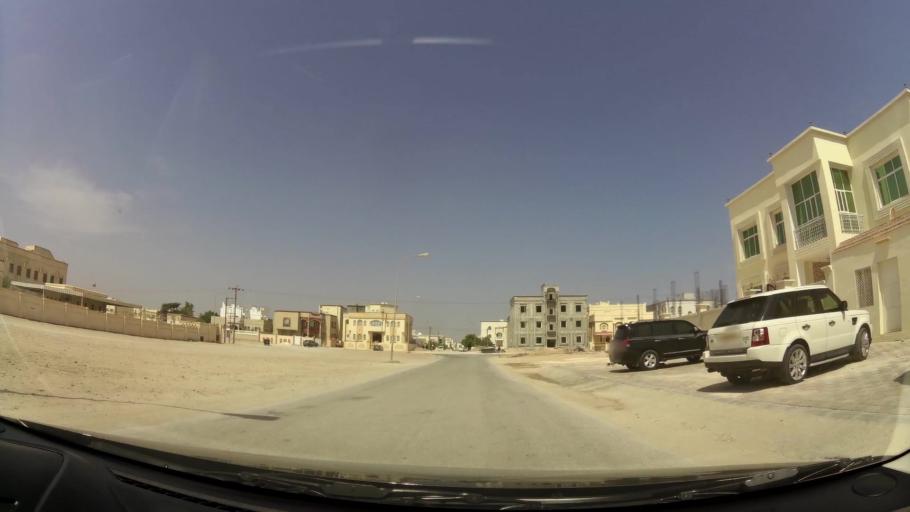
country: OM
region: Zufar
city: Salalah
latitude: 17.0434
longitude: 54.1537
